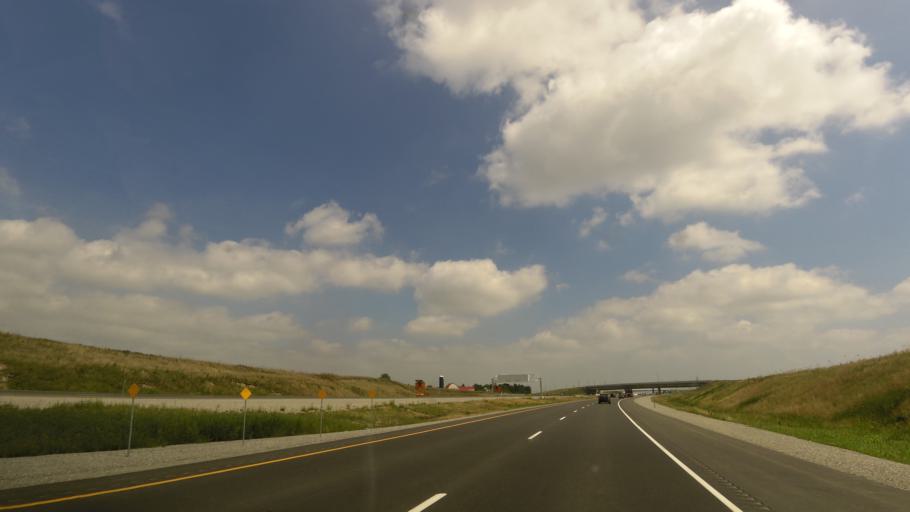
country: CA
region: Ontario
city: Ajax
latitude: 43.9511
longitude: -78.9831
